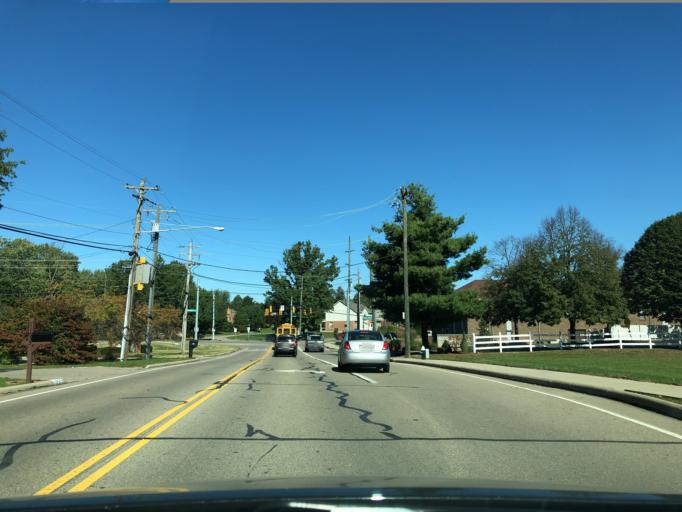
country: US
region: Ohio
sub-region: Hamilton County
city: Sixteen Mile Stand
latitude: 39.2845
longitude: -84.3102
